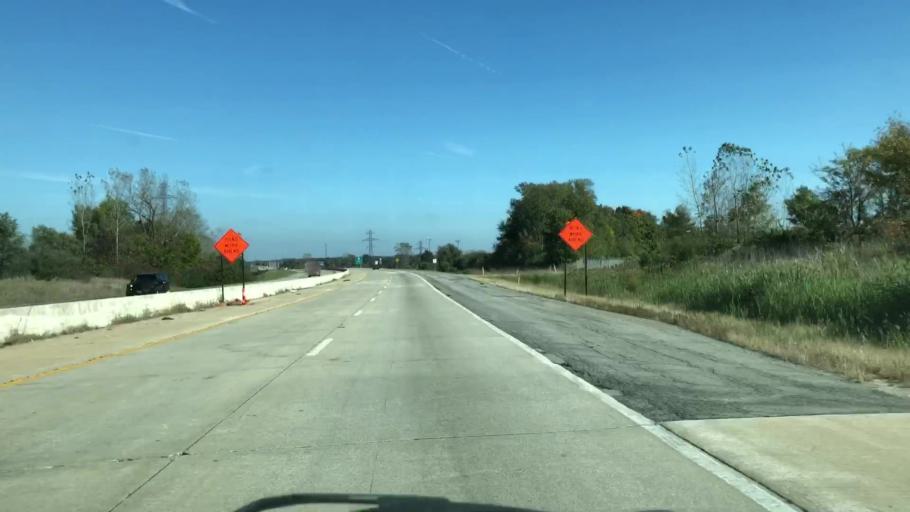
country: US
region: Indiana
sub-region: Elkhart County
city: Elkhart
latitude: 41.6393
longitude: -85.9702
